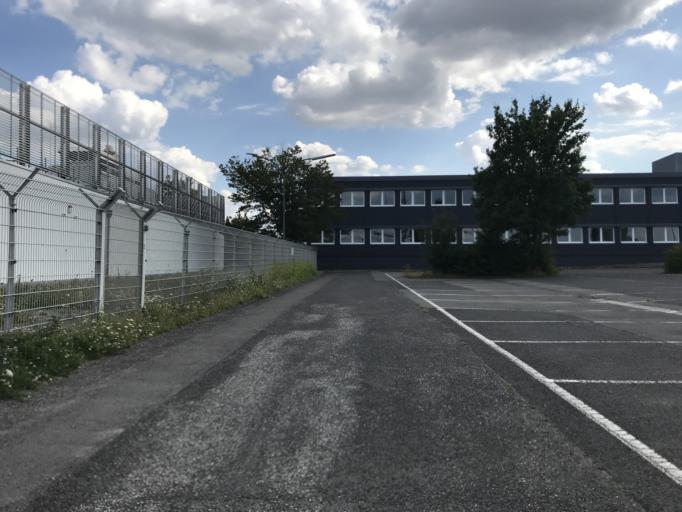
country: DE
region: Rheinland-Pfalz
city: Mainz
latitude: 49.9780
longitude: 8.2822
